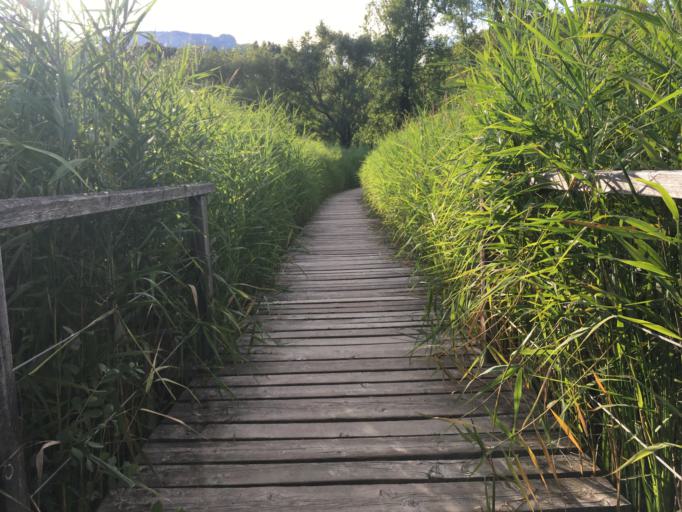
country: IT
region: Trentino-Alto Adige
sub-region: Bolzano
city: Vadena
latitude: 46.4204
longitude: 11.2858
